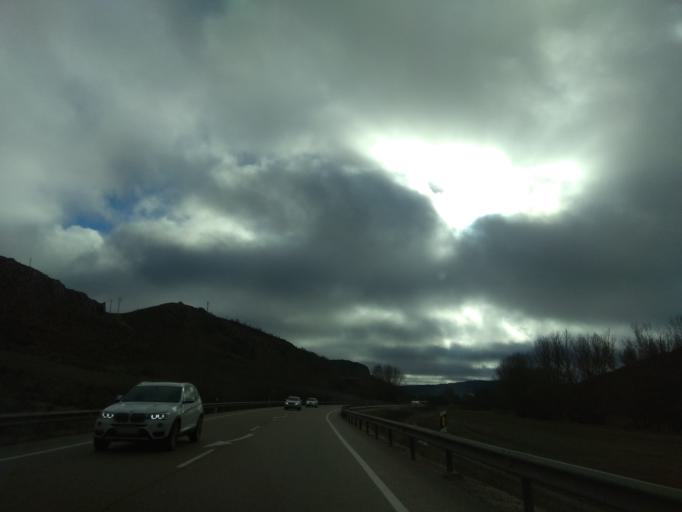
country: ES
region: Castille and Leon
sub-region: Provincia de Burgos
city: Montorio
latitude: 42.5764
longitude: -3.7766
